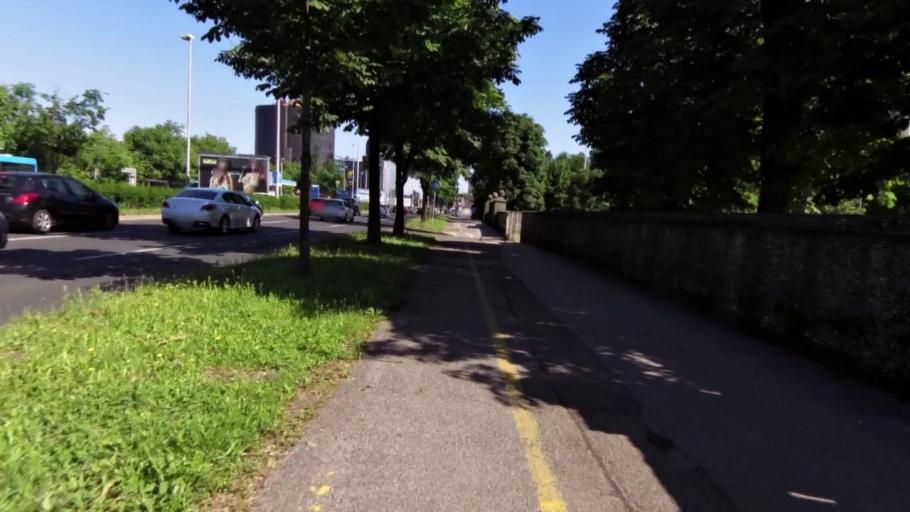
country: HR
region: Grad Zagreb
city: Zagreb
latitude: 45.8040
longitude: 16.0087
